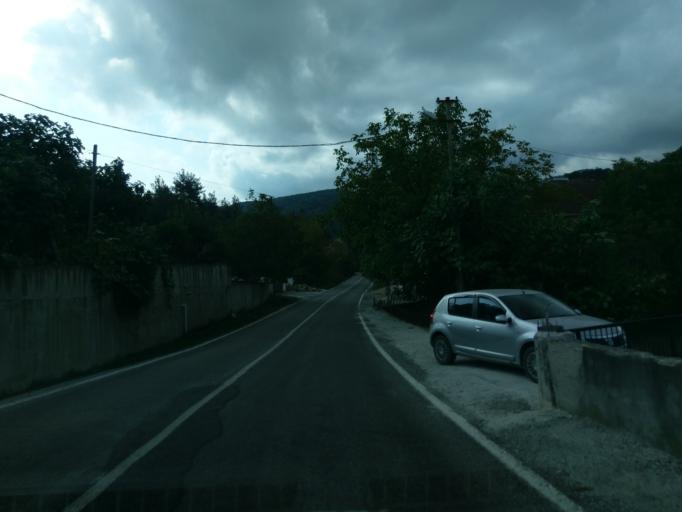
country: TR
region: Sinop
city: Helaldi
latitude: 41.9153
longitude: 34.4208
